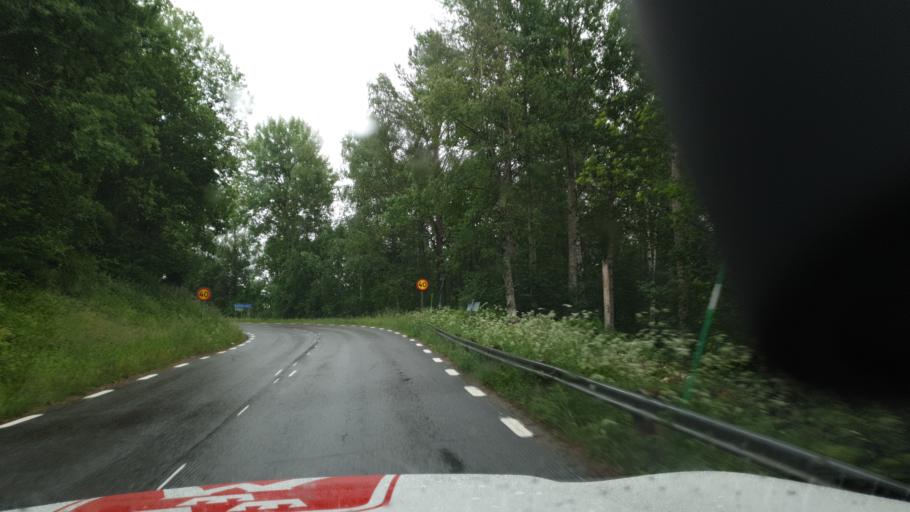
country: SE
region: Vaesterbotten
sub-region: Umea Kommun
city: Roback
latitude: 63.8738
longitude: 20.0564
